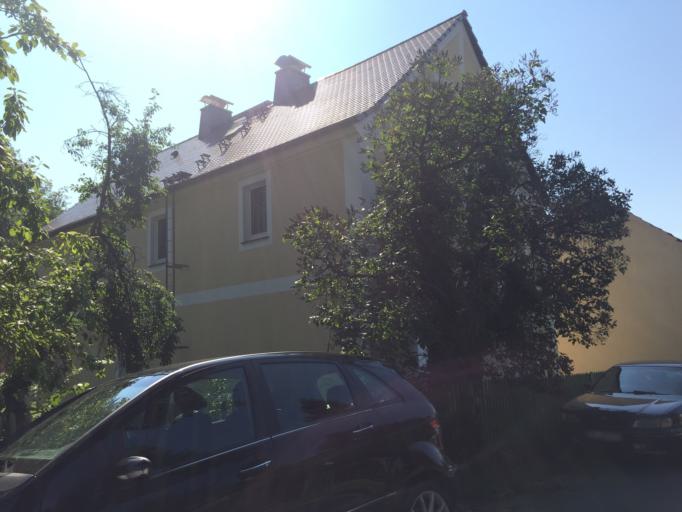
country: DE
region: Saxony
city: Uhyst
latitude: 51.3662
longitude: 14.5111
